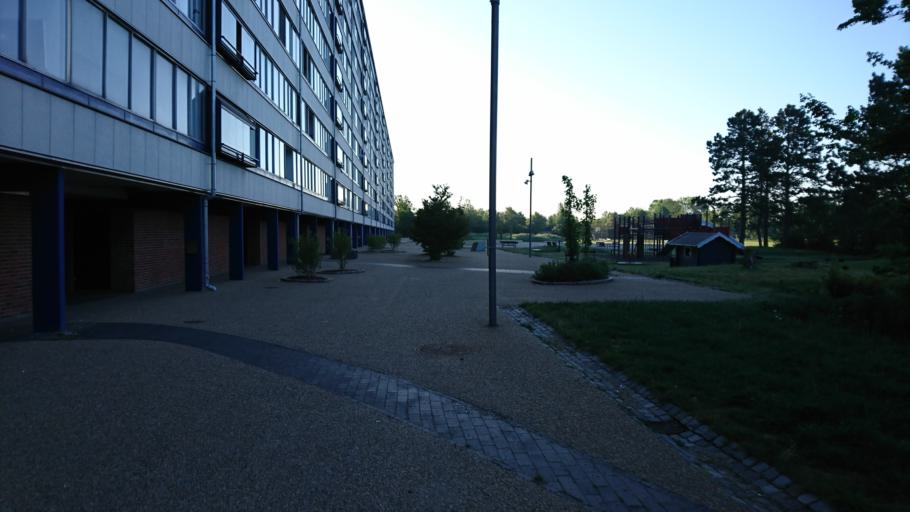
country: DK
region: Capital Region
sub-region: Ballerup Kommune
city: Ballerup
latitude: 55.7271
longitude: 12.3363
